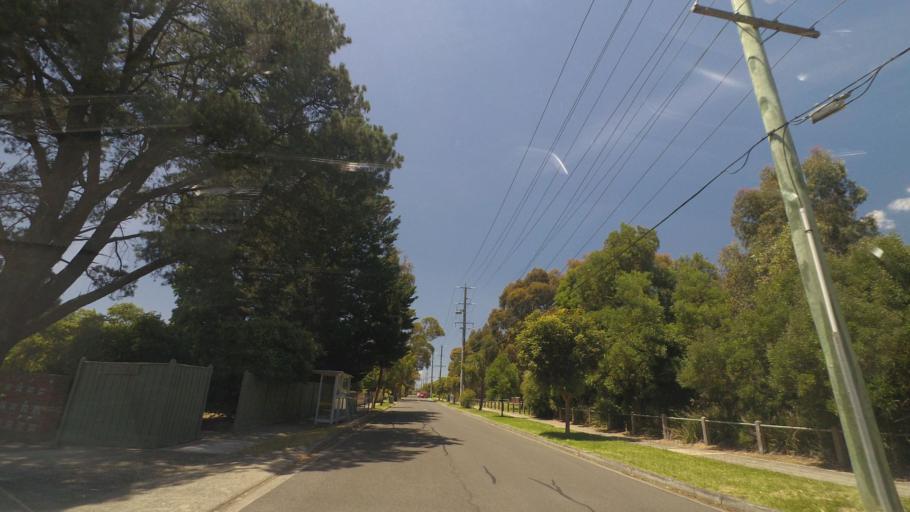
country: AU
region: Victoria
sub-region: Knox
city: Bayswater
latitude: -37.8339
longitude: 145.2730
